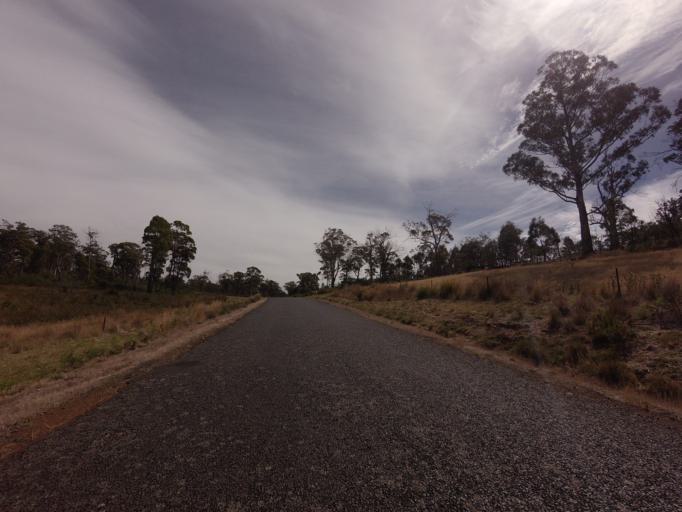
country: AU
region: Tasmania
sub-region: Sorell
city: Sorell
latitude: -42.5563
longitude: 147.6789
